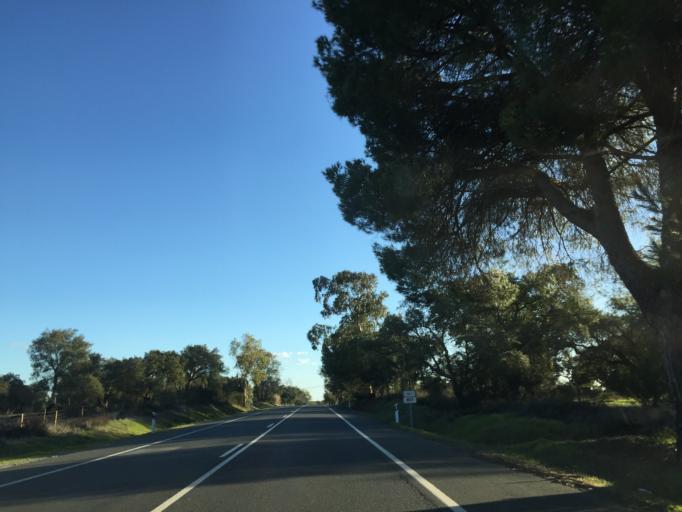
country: PT
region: Setubal
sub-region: Grandola
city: Grandola
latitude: 38.0280
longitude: -8.3999
